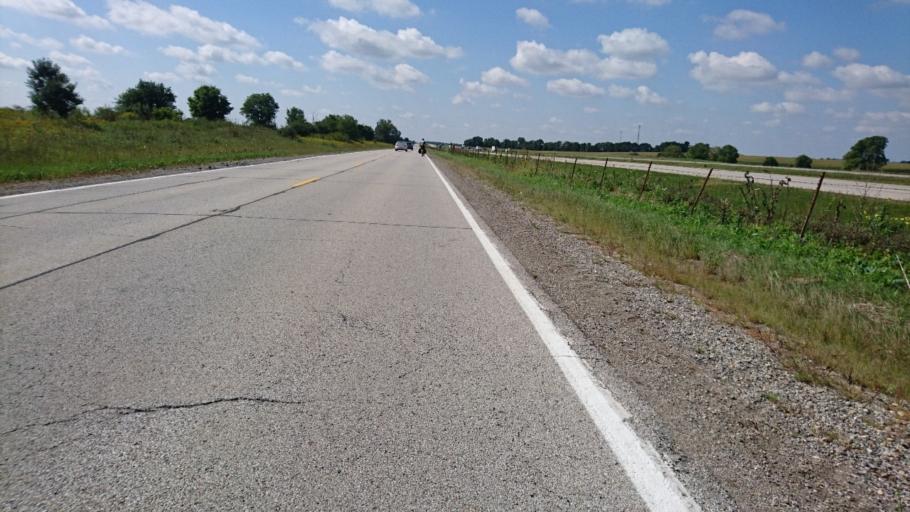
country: US
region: Illinois
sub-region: McLean County
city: Lexington
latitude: 40.6032
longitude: -88.8410
